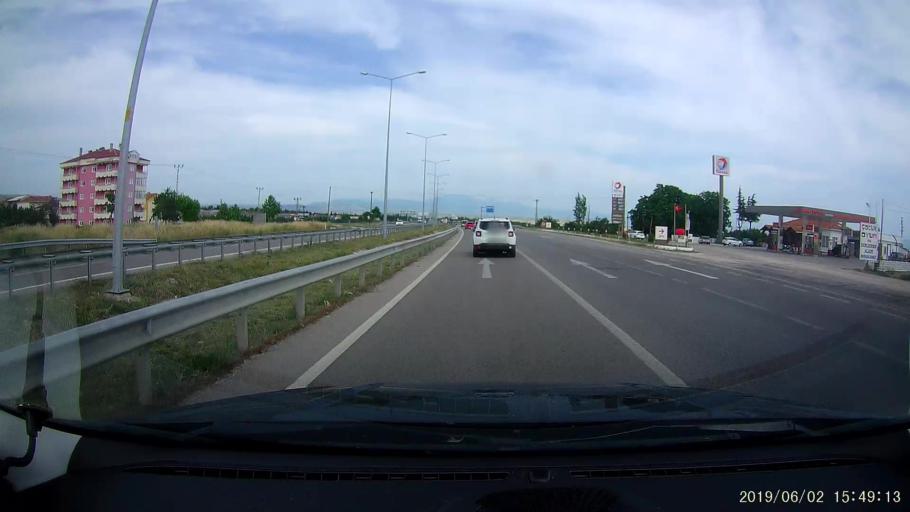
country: TR
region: Amasya
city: Merzifon
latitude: 40.8578
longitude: 35.4605
